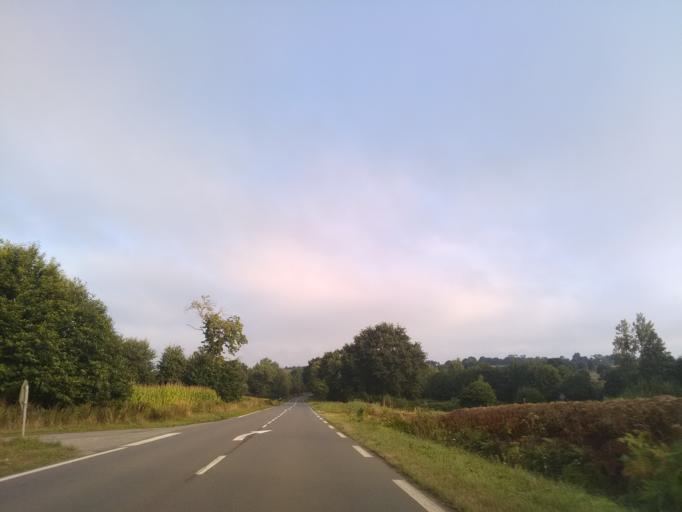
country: FR
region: Brittany
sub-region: Departement d'Ille-et-Vilaine
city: Geveze
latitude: 48.2320
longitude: -1.8029
